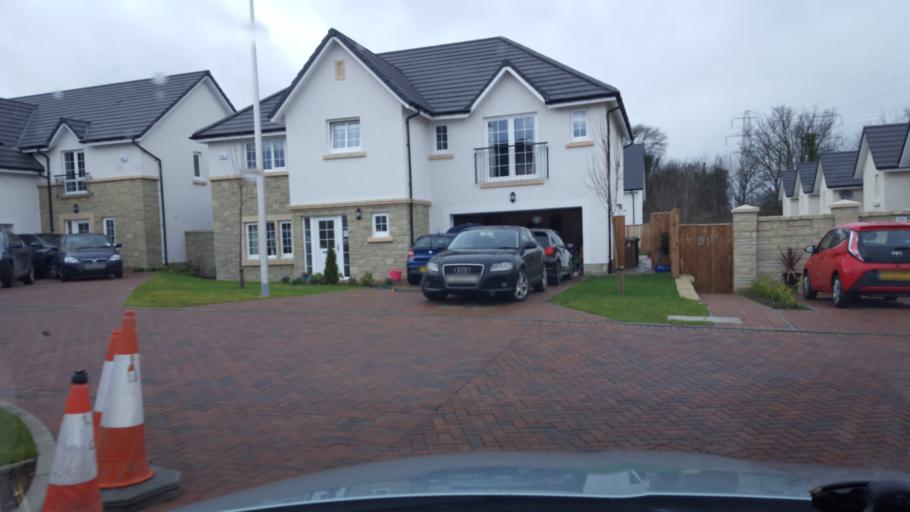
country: GB
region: Scotland
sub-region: Edinburgh
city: Currie
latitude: 55.9014
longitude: -3.3109
